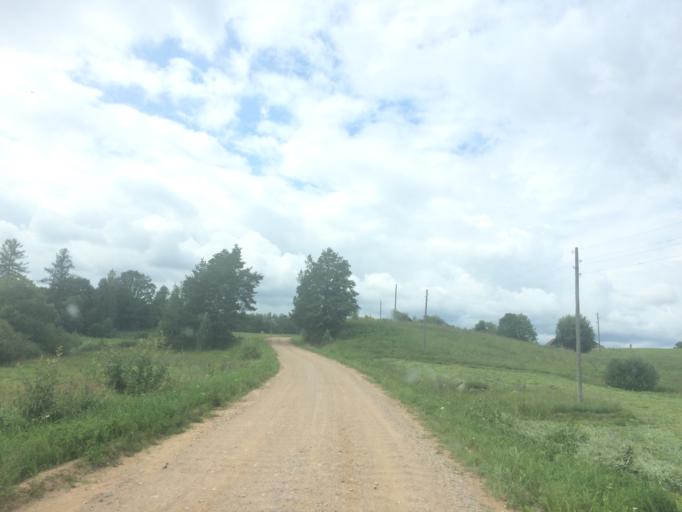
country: LV
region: Rezekne
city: Rezekne
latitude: 56.6581
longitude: 27.2723
